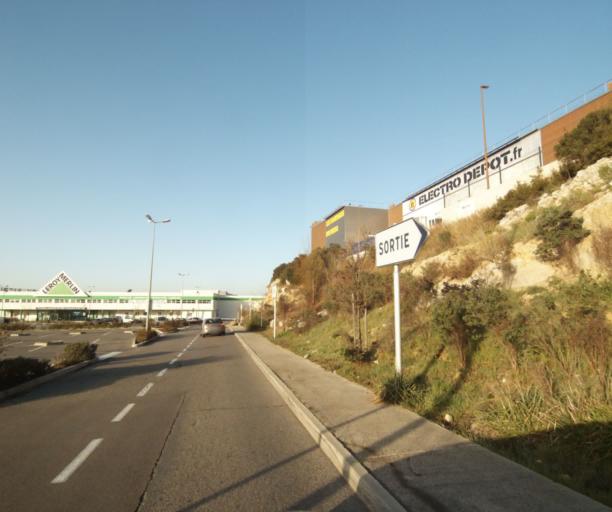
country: FR
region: Provence-Alpes-Cote d'Azur
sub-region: Departement des Bouches-du-Rhone
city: Cabries
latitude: 43.4248
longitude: 5.3681
